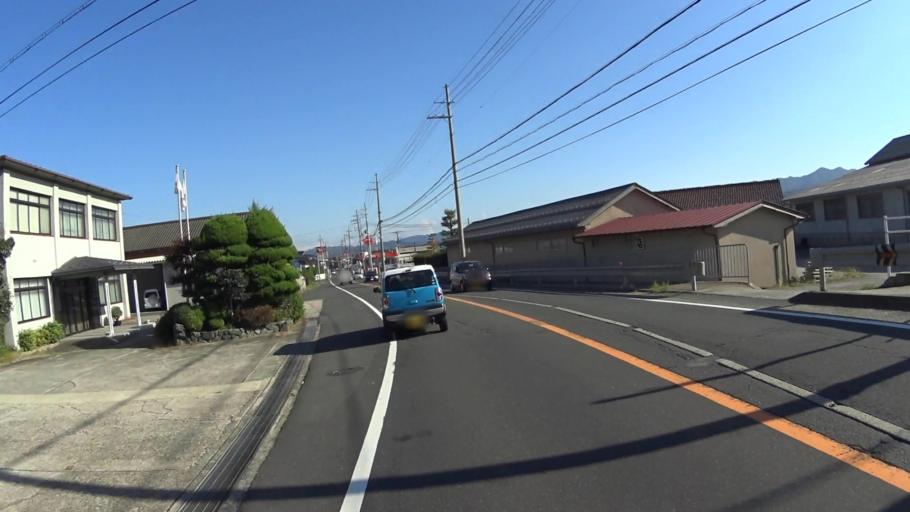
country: JP
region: Kyoto
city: Miyazu
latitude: 35.6147
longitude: 135.0608
